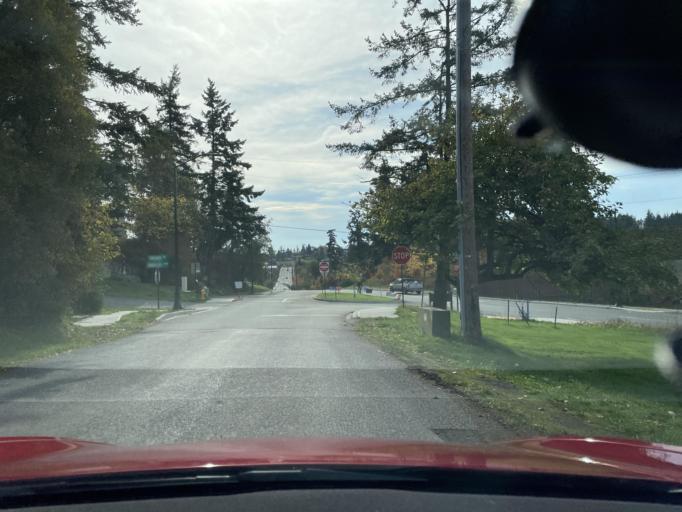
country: US
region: Washington
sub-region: San Juan County
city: Friday Harbor
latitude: 48.5423
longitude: -123.0232
